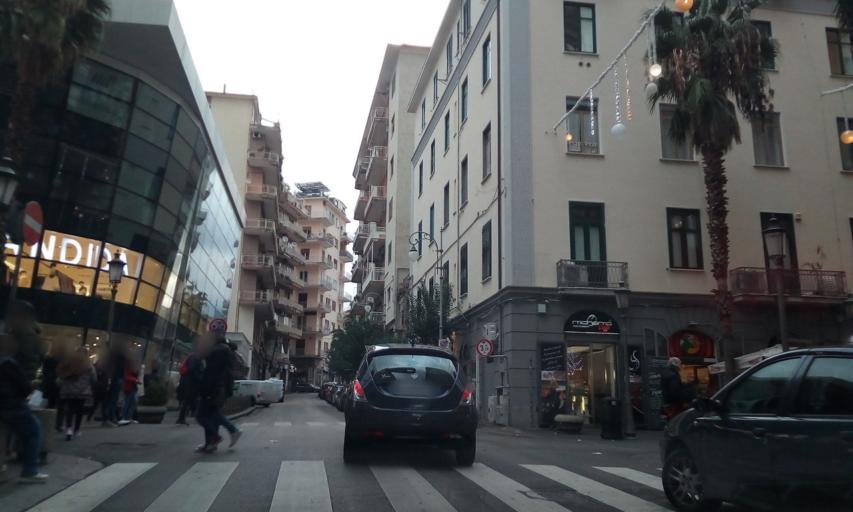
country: IT
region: Campania
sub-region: Provincia di Salerno
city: Salerno
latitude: 40.6759
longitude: 14.7688
